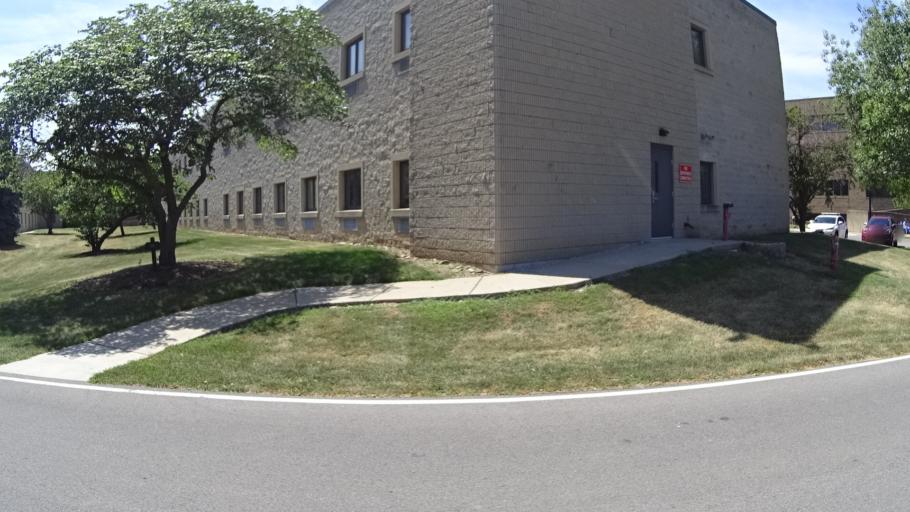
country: US
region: Ohio
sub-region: Erie County
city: Sandusky
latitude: 41.4203
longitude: -82.6828
